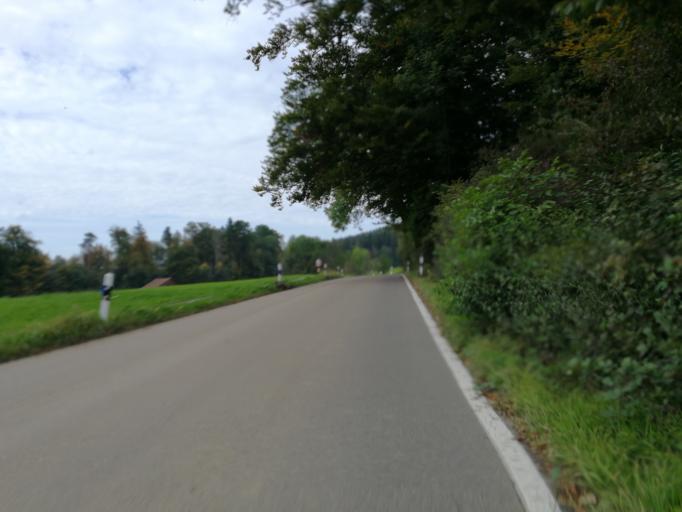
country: CH
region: Zurich
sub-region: Bezirk Meilen
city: Oetwil am See
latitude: 47.2615
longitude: 8.7164
